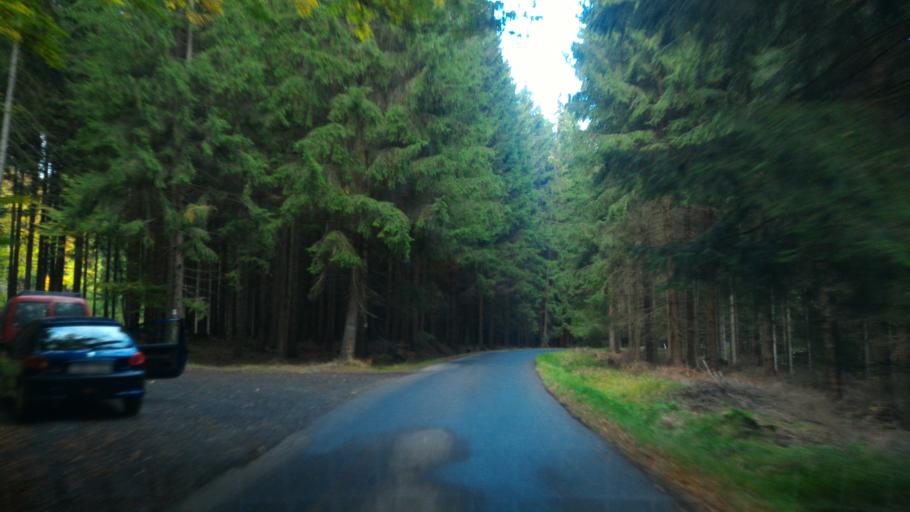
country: CZ
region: Ustecky
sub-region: Okres Decin
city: Chribska
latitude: 50.8182
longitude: 14.4843
